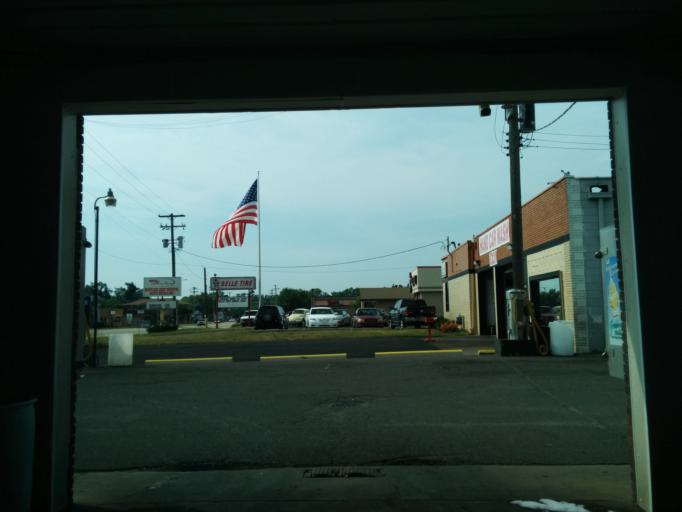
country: US
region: Michigan
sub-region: Oakland County
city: Farmington
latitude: 42.4595
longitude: -83.3569
